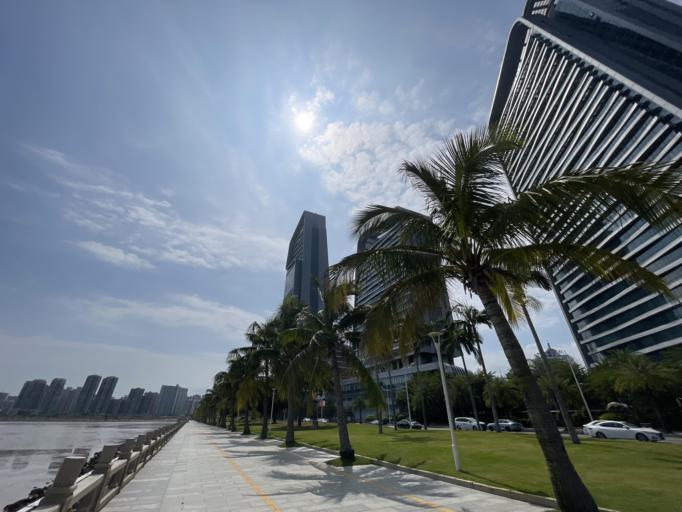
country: MO
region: Macau
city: Macau
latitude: 22.2236
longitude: 113.5555
